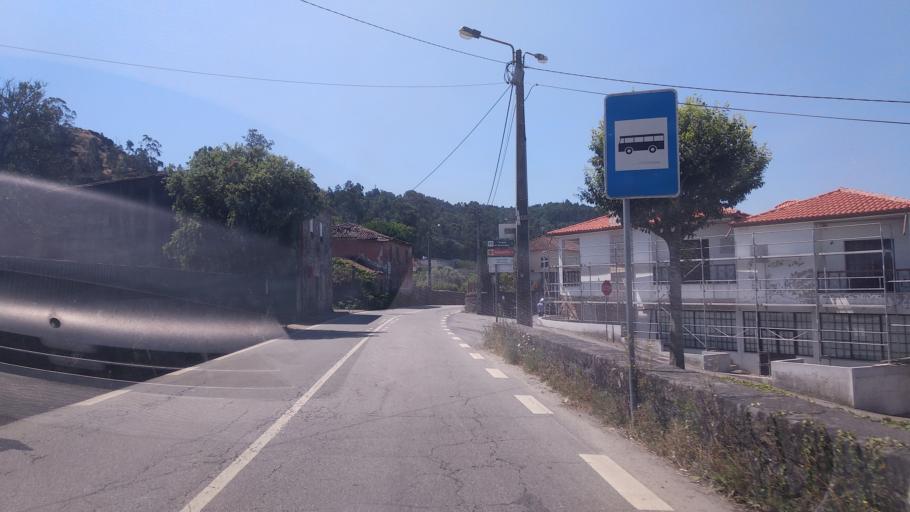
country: PT
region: Braga
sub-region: Braga
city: Adaufe
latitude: 41.5848
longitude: -8.4044
